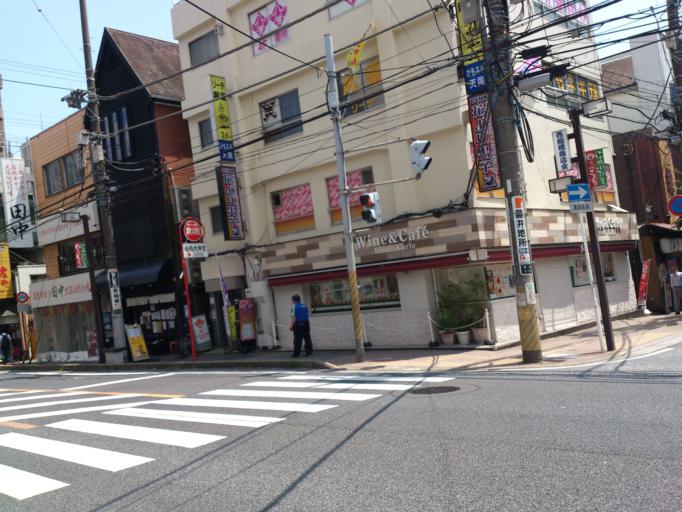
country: JP
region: Chiba
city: Funabashi
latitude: 35.7089
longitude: 139.9598
